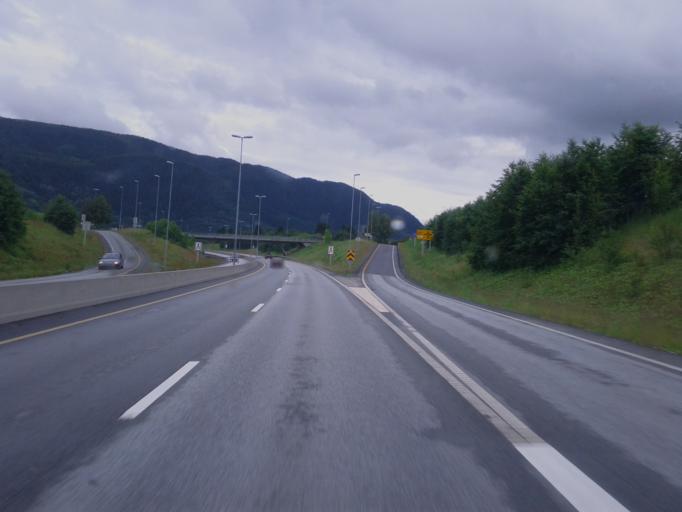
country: NO
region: Sor-Trondelag
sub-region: Melhus
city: Melhus
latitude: 63.2831
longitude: 10.2731
